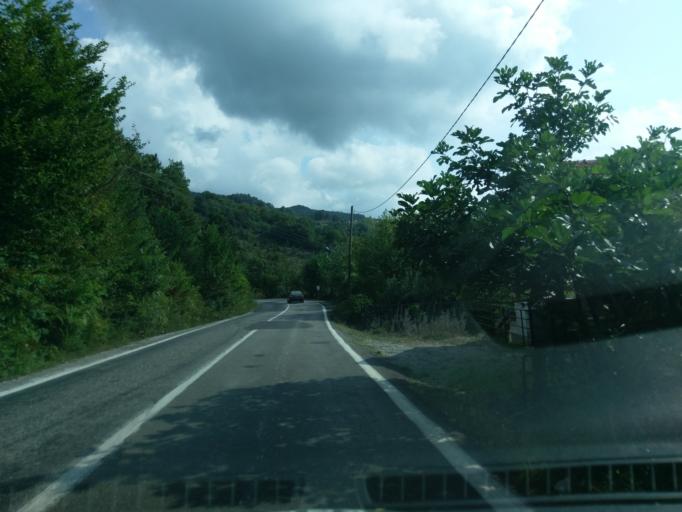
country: TR
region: Sinop
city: Ayancik
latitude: 41.8792
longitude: 34.5316
